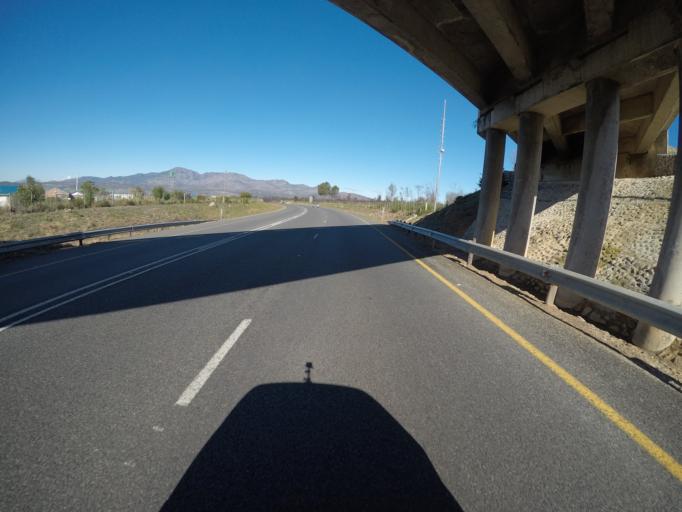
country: ZA
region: Western Cape
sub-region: Overberg District Municipality
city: Grabouw
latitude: -34.2307
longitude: 19.1878
